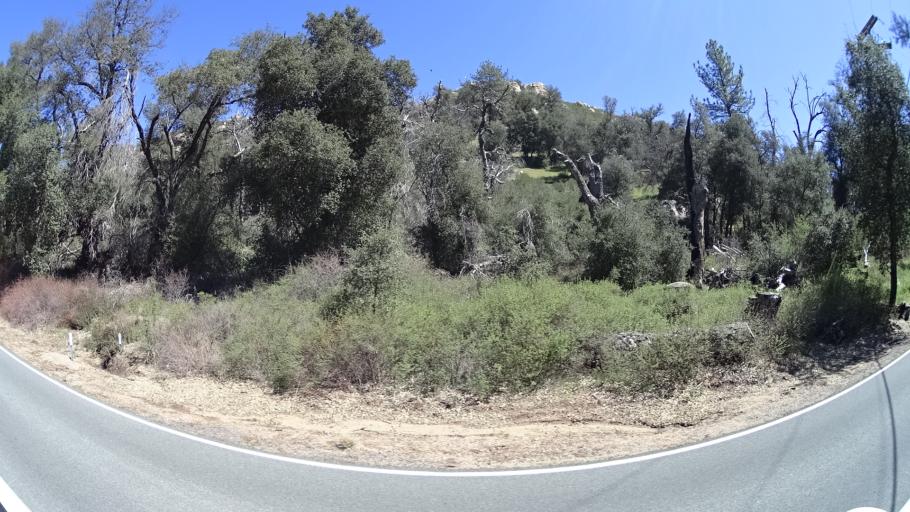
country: US
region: California
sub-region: San Diego County
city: Descanso
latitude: 32.9008
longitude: -116.5806
